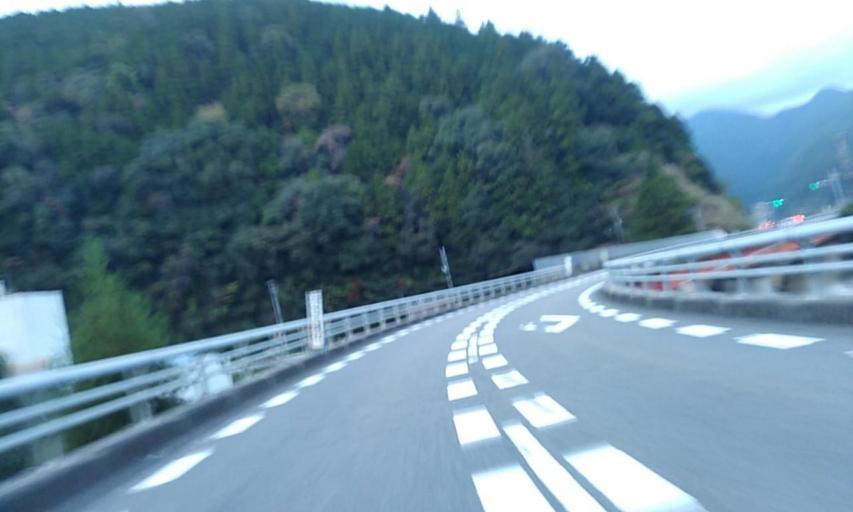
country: JP
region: Wakayama
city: Shingu
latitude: 33.7430
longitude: 135.9379
